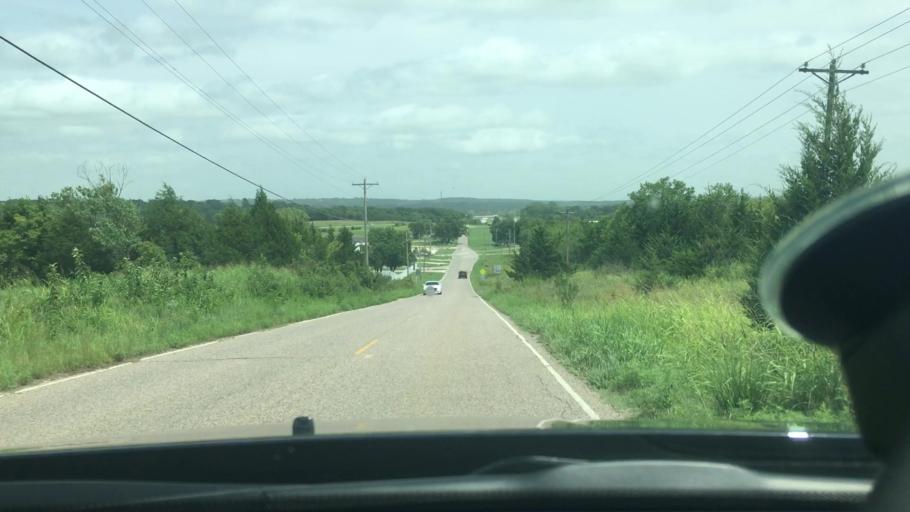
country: US
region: Oklahoma
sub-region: Pontotoc County
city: Ada
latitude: 34.7527
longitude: -96.6922
